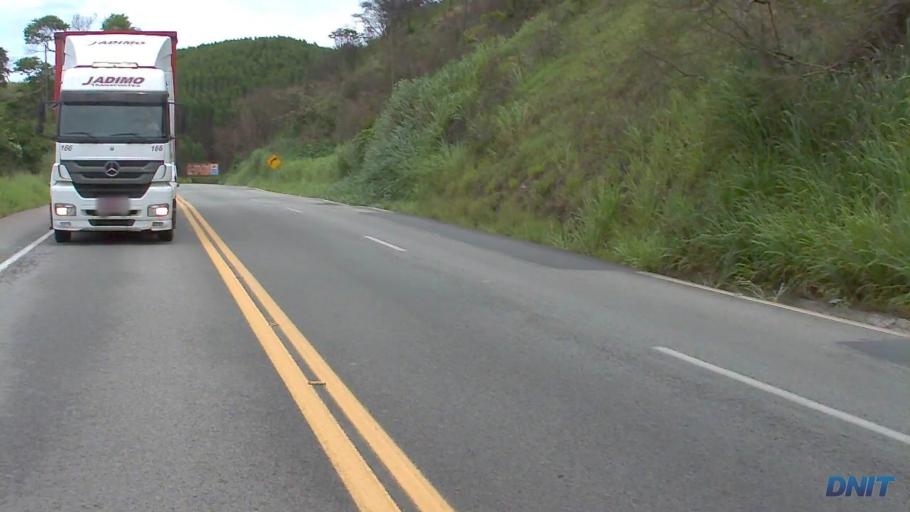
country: BR
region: Minas Gerais
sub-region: Nova Era
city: Nova Era
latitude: -19.6696
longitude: -42.9685
